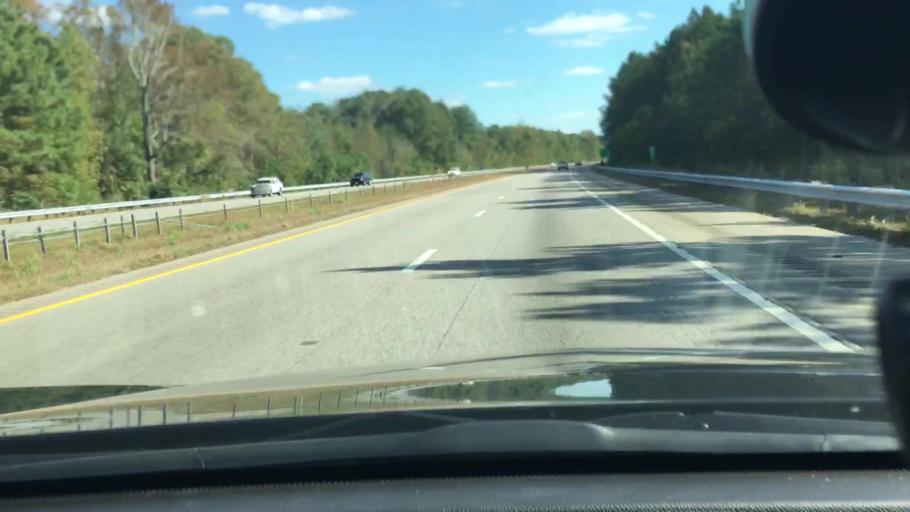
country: US
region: North Carolina
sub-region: Wilson County
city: Lucama
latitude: 35.7022
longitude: -77.9836
